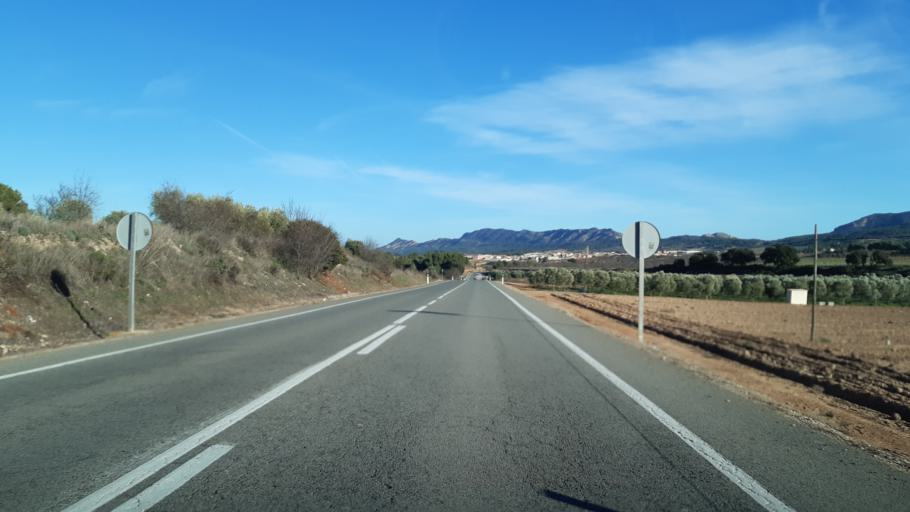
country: ES
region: Catalonia
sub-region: Provincia de Tarragona
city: Gandesa
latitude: 41.0541
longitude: 0.4097
